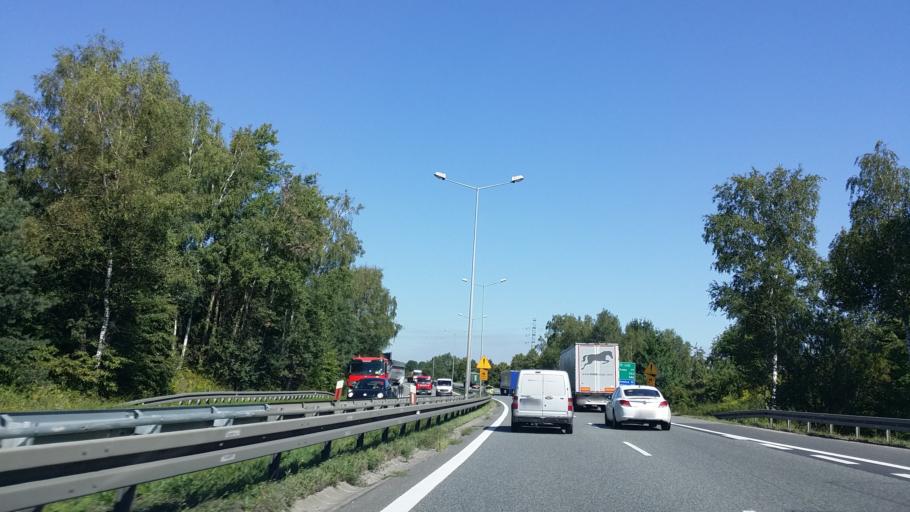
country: PL
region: Silesian Voivodeship
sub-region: Myslowice
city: Myslowice
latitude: 50.1975
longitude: 19.1688
